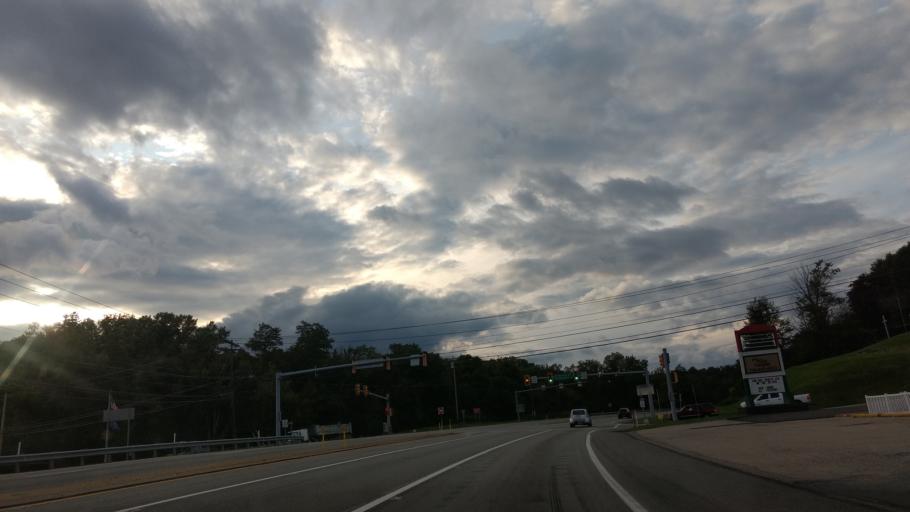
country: US
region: Pennsylvania
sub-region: Westmoreland County
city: Fellsburg
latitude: 40.1866
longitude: -79.8172
